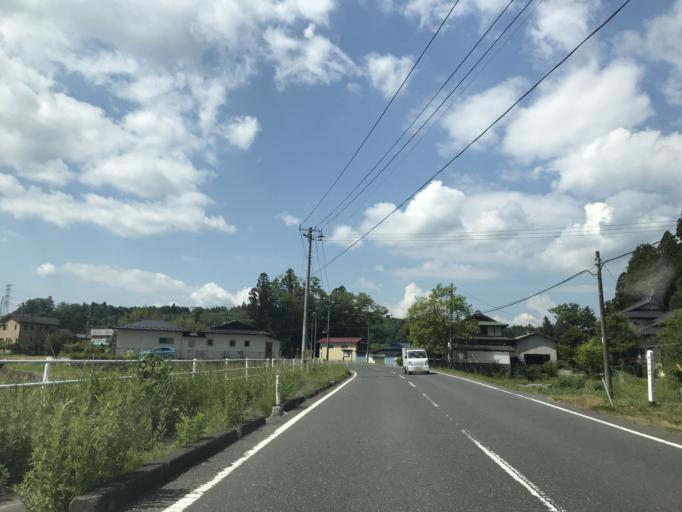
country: JP
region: Miyagi
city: Furukawa
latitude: 38.7868
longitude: 140.9586
